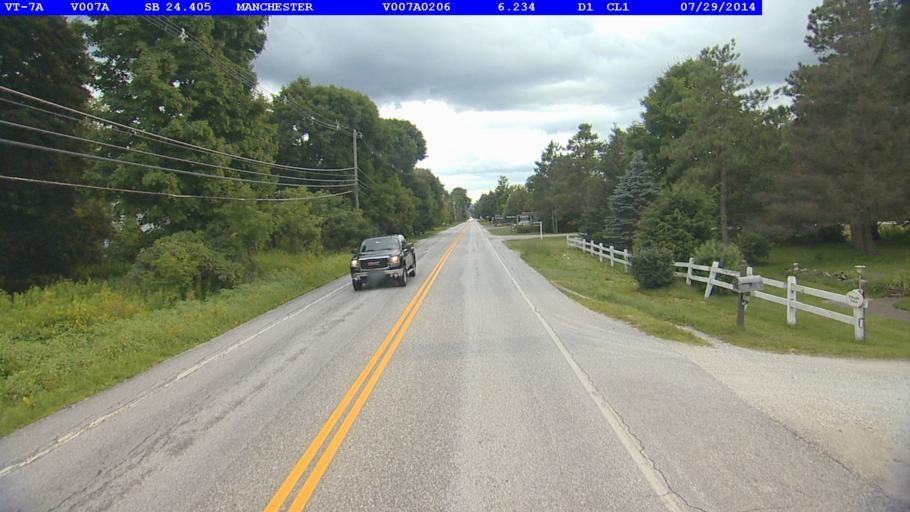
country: US
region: Vermont
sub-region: Bennington County
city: Manchester Center
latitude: 43.1910
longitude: -73.0420
